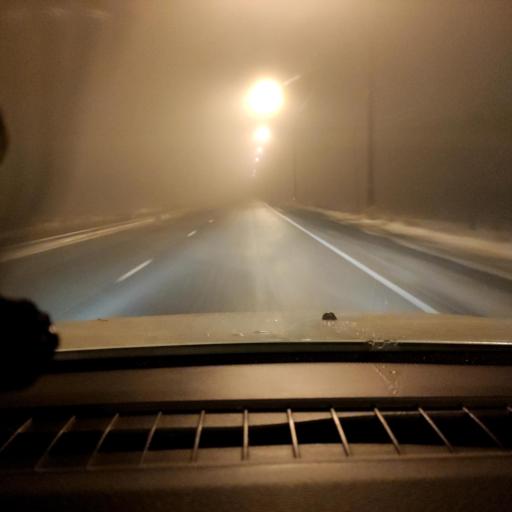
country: RU
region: Samara
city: Dubovyy Umet
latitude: 52.9644
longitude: 50.2861
